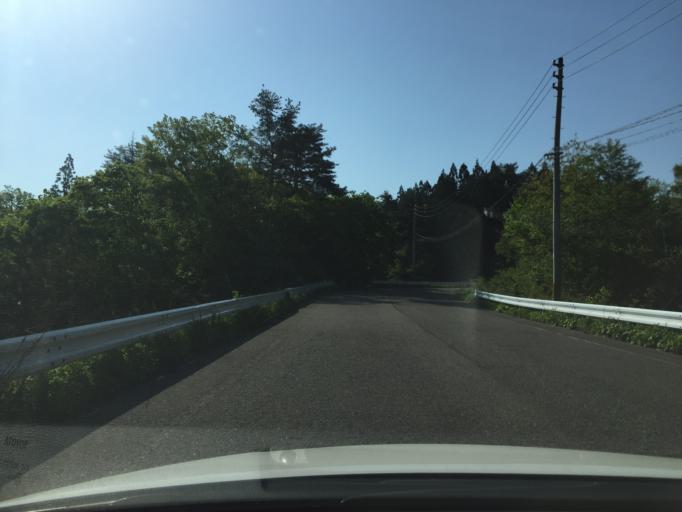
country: JP
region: Fukushima
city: Kitakata
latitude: 37.6741
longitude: 139.6342
